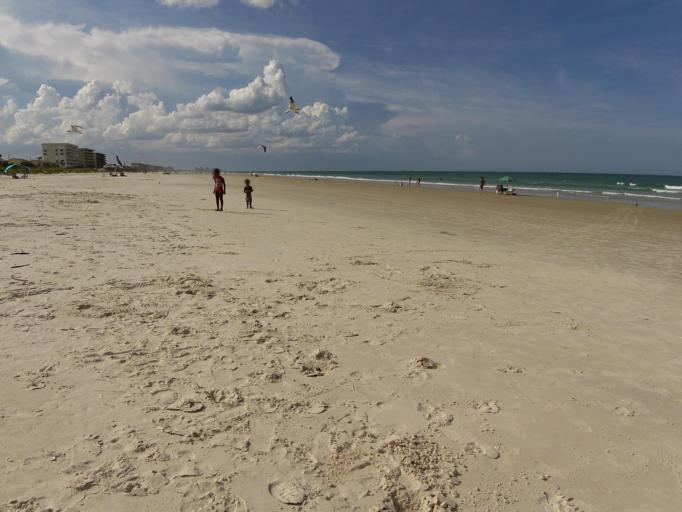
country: US
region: Florida
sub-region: Volusia County
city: Ponce Inlet
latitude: 29.0898
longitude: -80.9285
